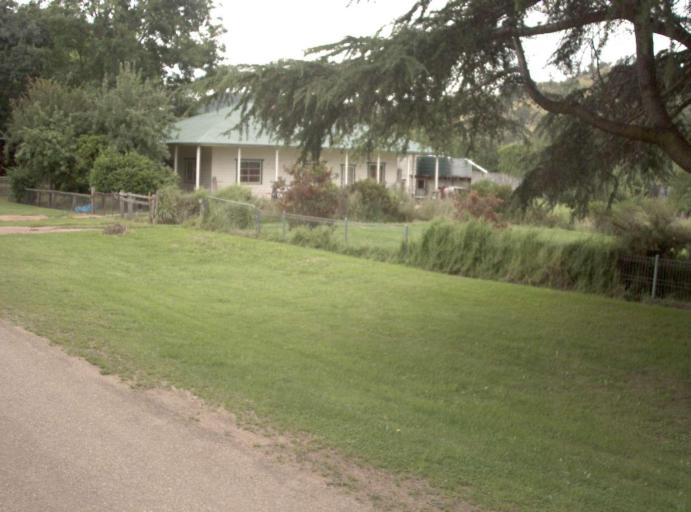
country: AU
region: Victoria
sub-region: East Gippsland
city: Bairnsdale
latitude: -37.4603
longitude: 147.2508
